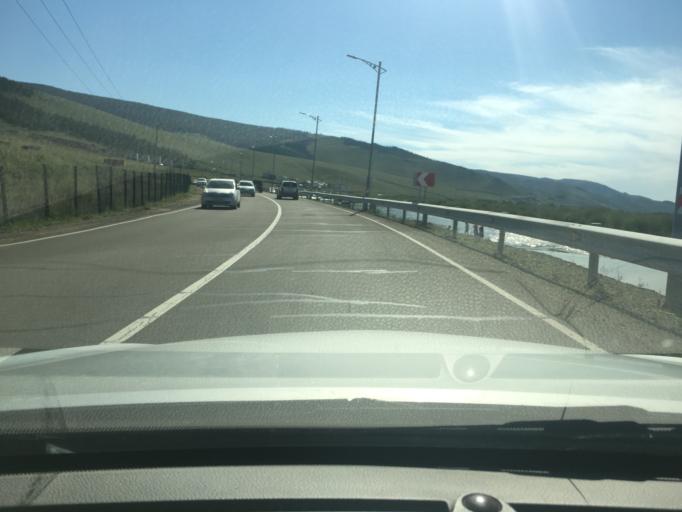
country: MN
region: Ulaanbaatar
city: Ulaanbaatar
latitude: 47.8909
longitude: 107.0299
